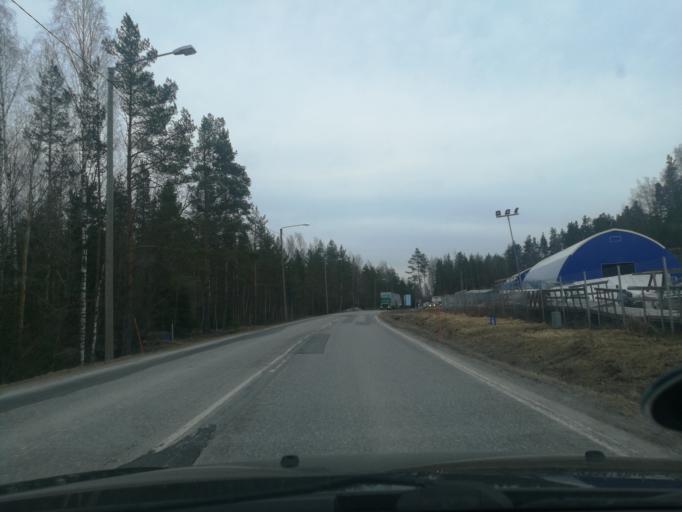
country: FI
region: Uusimaa
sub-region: Helsinki
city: Nickby
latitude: 60.2940
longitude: 25.3629
